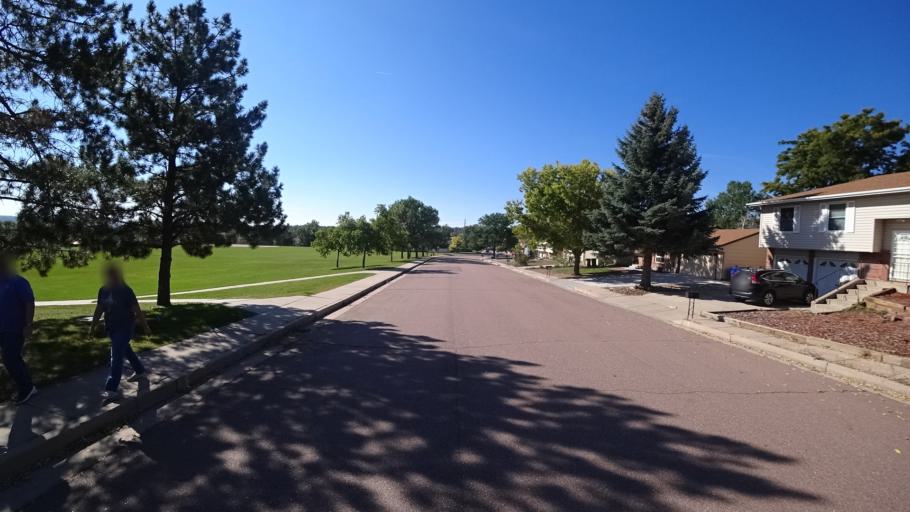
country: US
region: Colorado
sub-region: El Paso County
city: Colorado Springs
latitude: 38.9066
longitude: -104.7867
